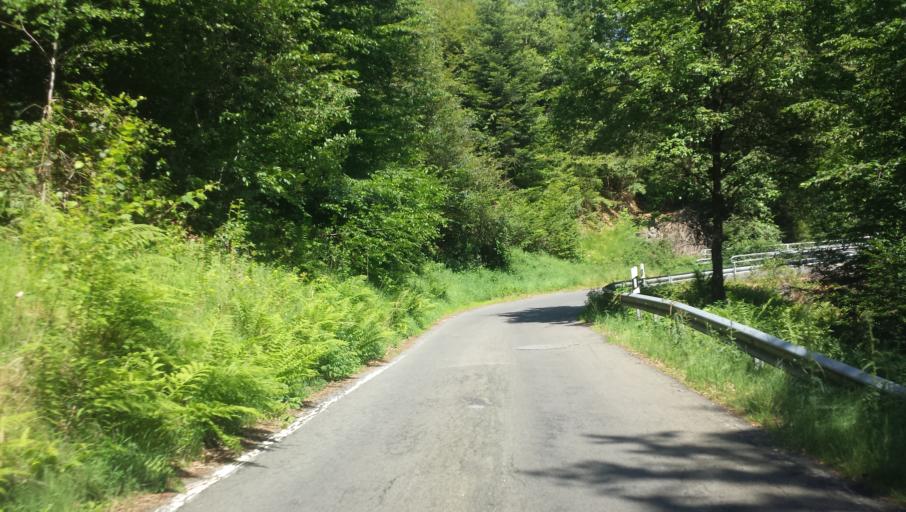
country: DE
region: Rheinland-Pfalz
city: Elmstein
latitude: 49.3674
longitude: 7.9204
